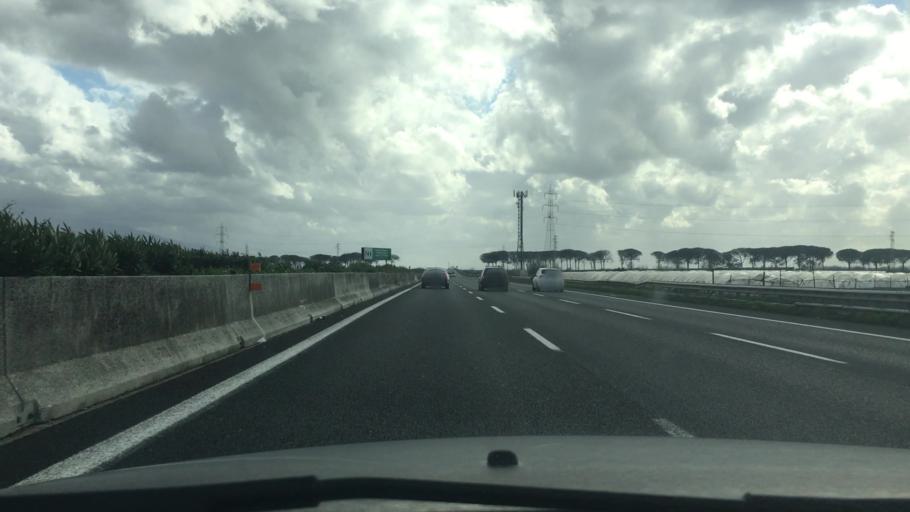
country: IT
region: Campania
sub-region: Provincia di Napoli
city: Pascarola
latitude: 40.9932
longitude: 14.3246
